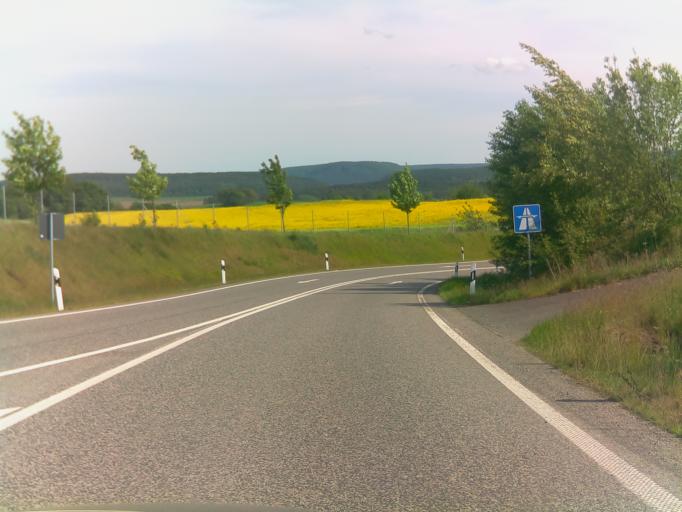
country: DE
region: Thuringia
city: Schachtebich
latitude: 51.3984
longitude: 10.0387
